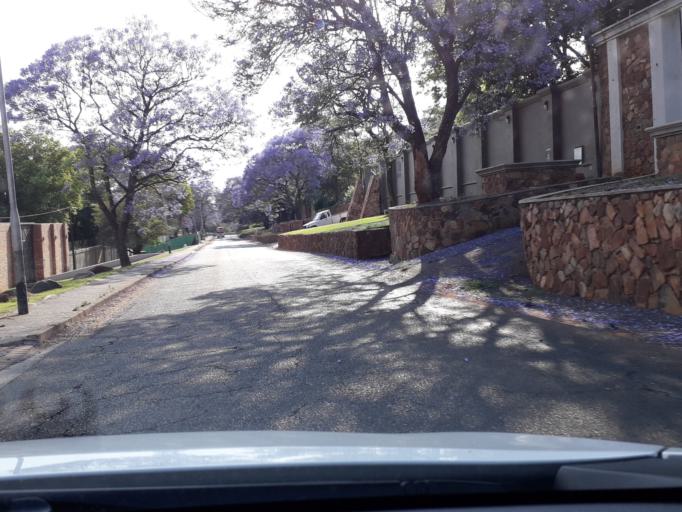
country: ZA
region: Gauteng
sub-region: City of Johannesburg Metropolitan Municipality
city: Roodepoort
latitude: -26.1409
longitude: 27.9641
